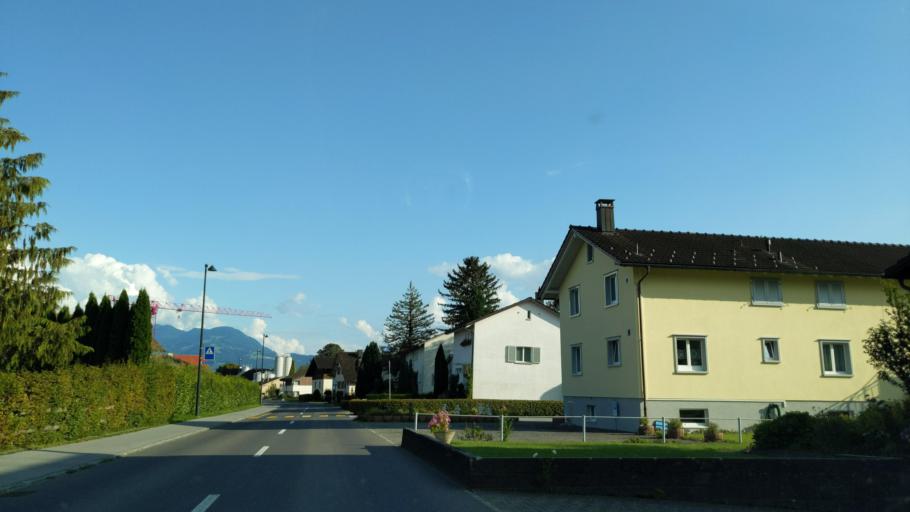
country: CH
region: Saint Gallen
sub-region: Wahlkreis Rheintal
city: Oberriet
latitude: 47.3273
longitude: 9.5643
